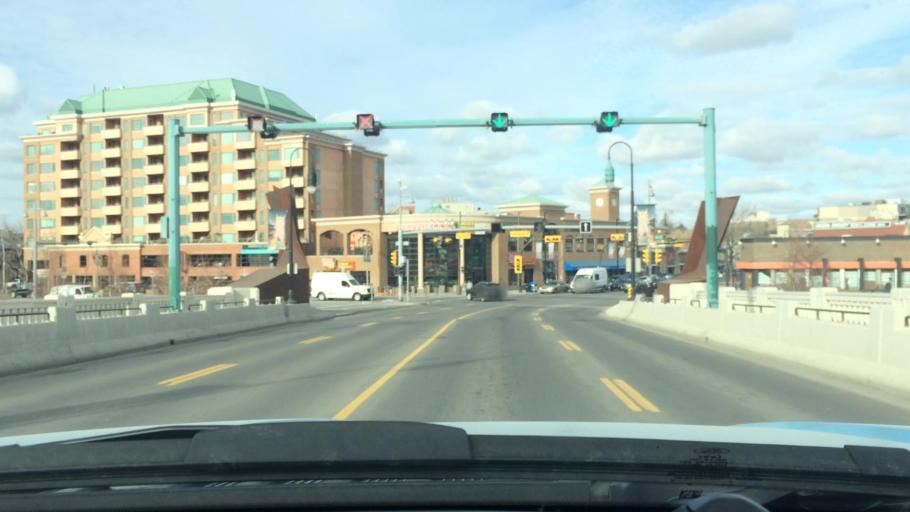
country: CA
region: Alberta
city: Calgary
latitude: 51.0514
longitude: -114.0852
